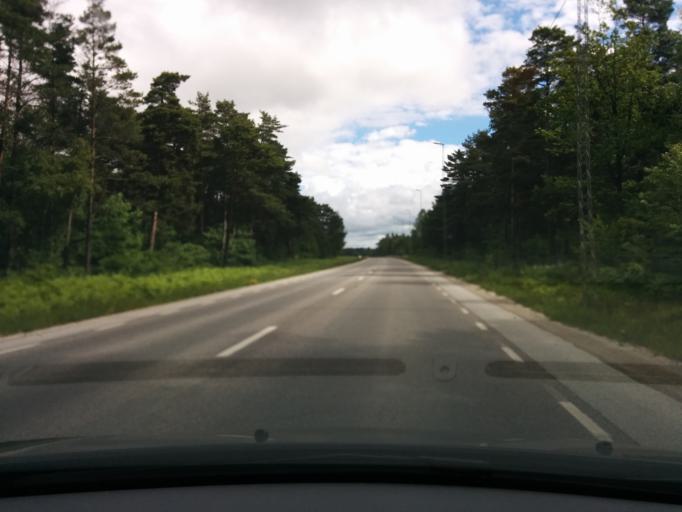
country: SE
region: Gotland
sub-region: Gotland
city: Visby
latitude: 57.6101
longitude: 18.3032
